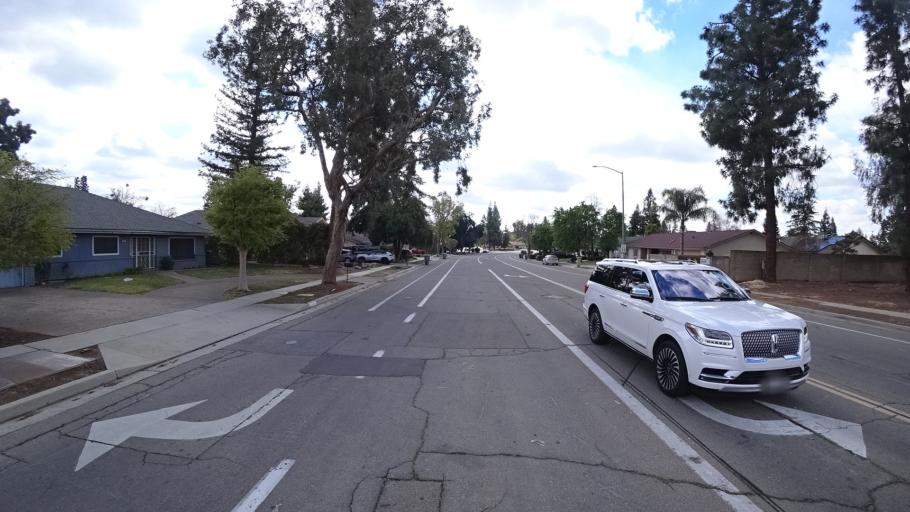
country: US
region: California
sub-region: Fresno County
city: Fresno
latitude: 36.8369
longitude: -119.8534
